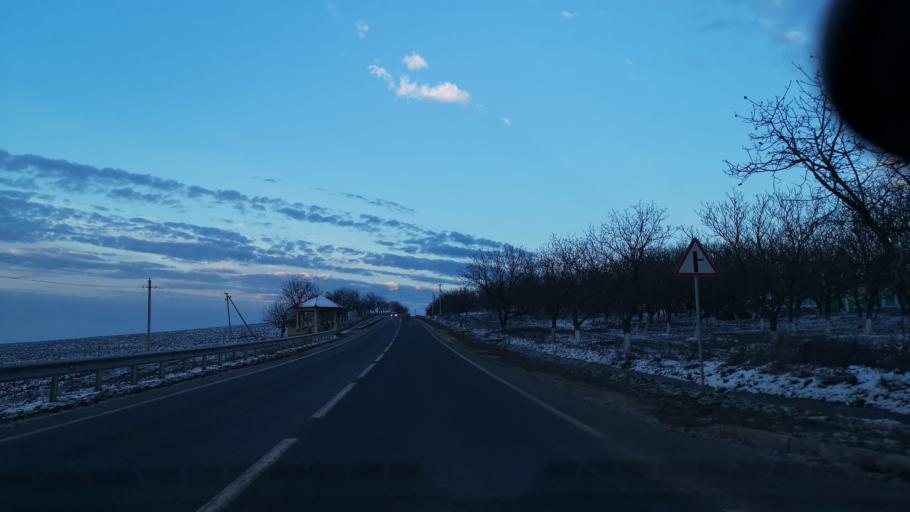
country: MD
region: Rezina
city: Saharna
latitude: 47.5919
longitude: 28.8222
